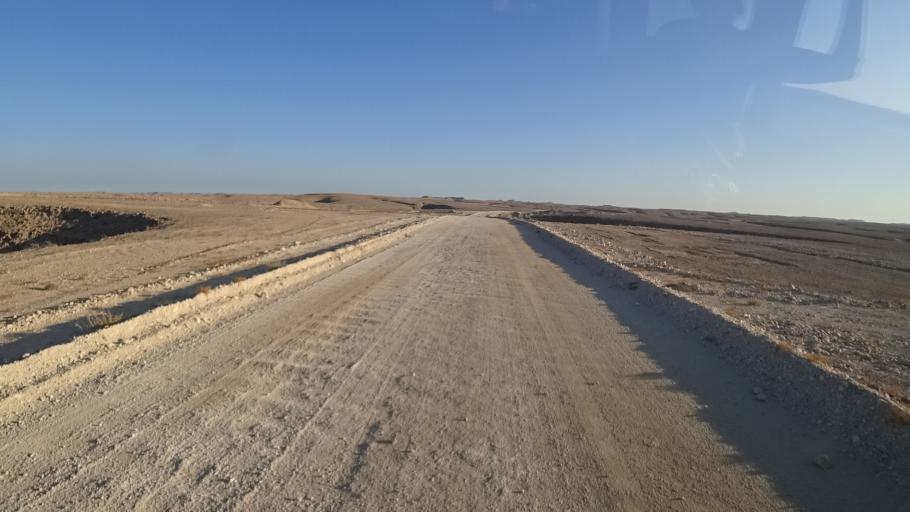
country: YE
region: Al Mahrah
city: Hawf
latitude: 17.1837
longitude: 53.3432
